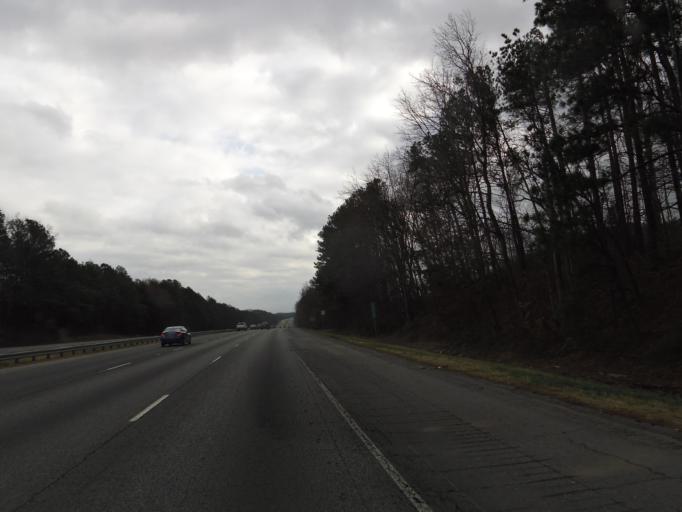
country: US
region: Georgia
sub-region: Gordon County
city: Calhoun
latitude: 34.6176
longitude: -84.9654
